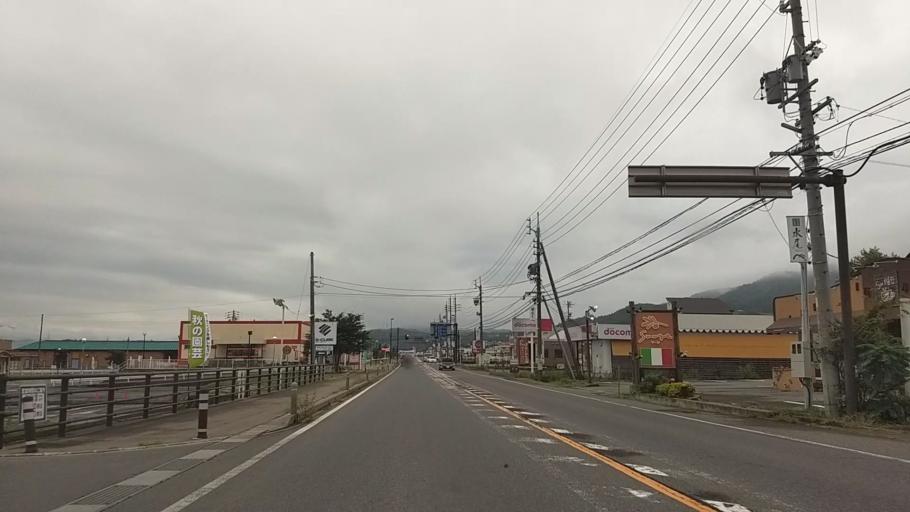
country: JP
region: Nagano
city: Iiyama
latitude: 36.8361
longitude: 138.3581
